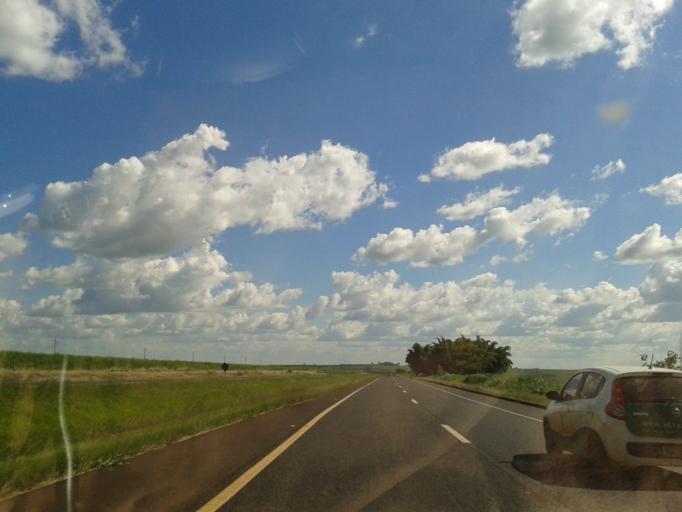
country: BR
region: Goias
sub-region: Morrinhos
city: Morrinhos
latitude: -17.8569
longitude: -49.2224
